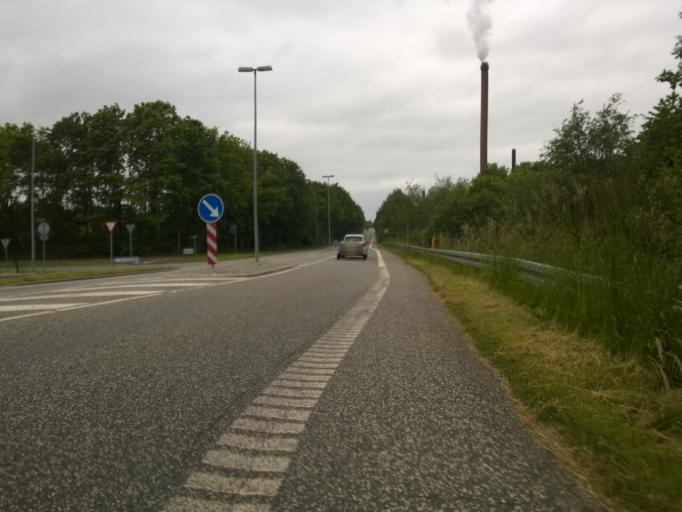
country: DK
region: Central Jutland
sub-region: Holstebro Kommune
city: Vinderup
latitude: 56.4762
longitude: 8.7966
